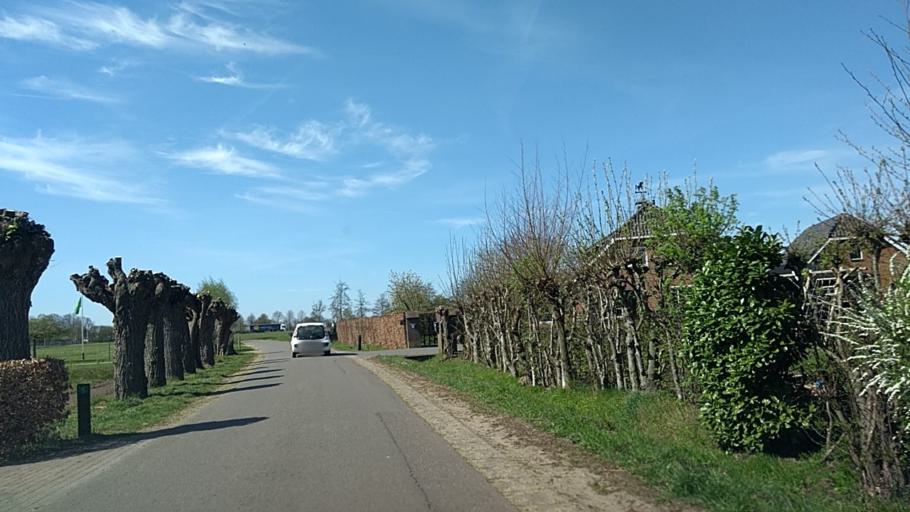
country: NL
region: Gelderland
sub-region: Gemeente Bronckhorst
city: Hengelo
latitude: 52.0201
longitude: 6.3035
